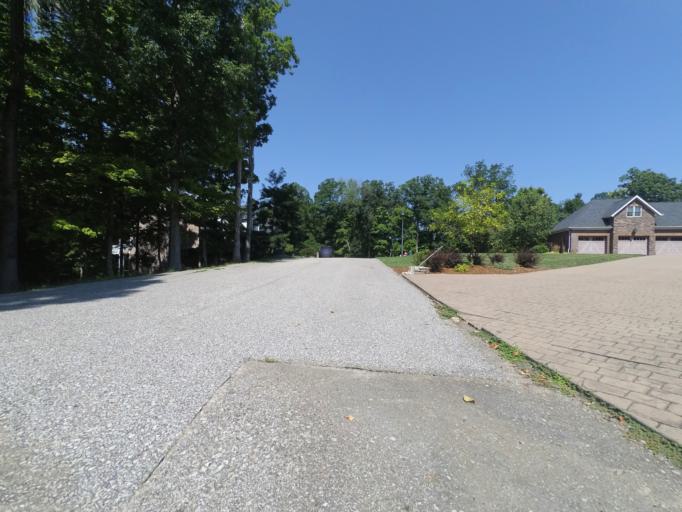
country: US
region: West Virginia
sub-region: Cabell County
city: Huntington
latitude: 38.3841
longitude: -82.4645
